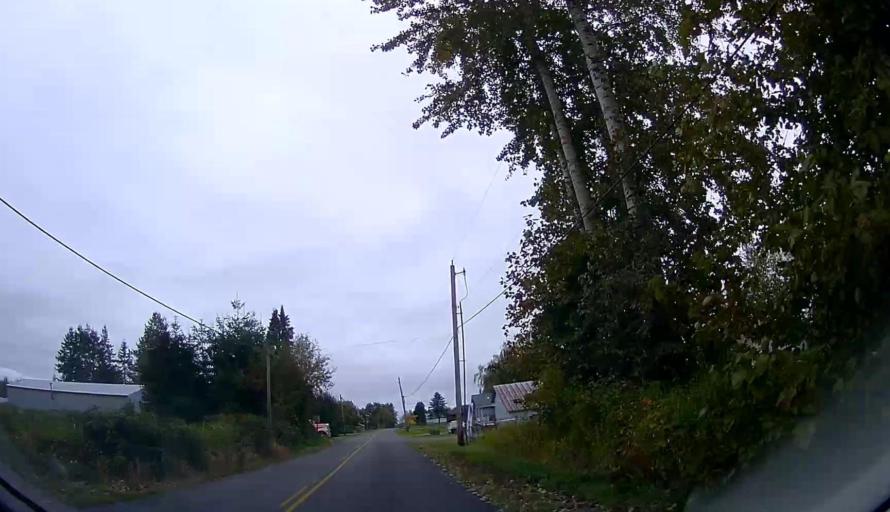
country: US
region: Washington
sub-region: Skagit County
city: Sedro-Woolley
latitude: 48.5144
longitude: -122.1710
